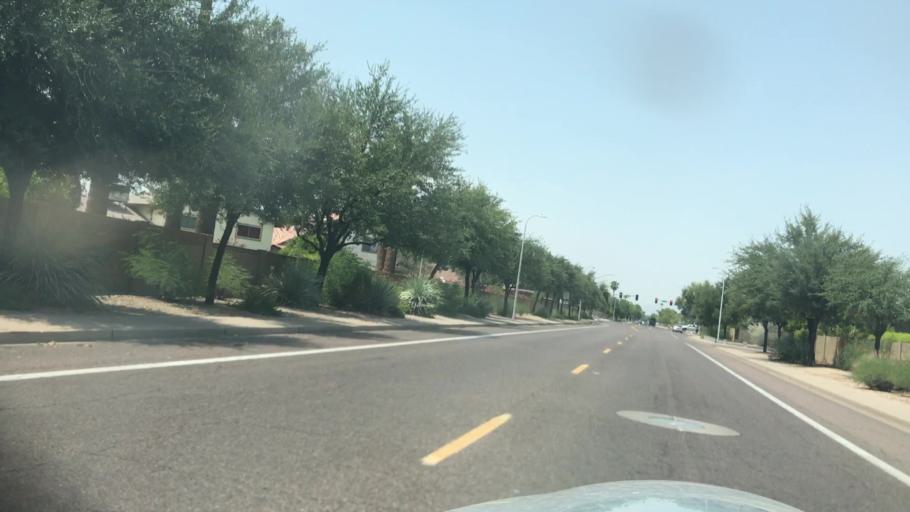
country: US
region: Arizona
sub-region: Maricopa County
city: Glendale
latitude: 33.5604
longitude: -112.1666
